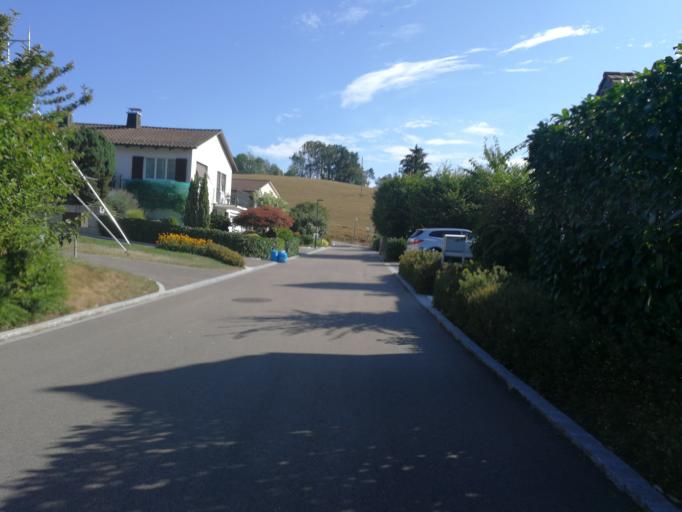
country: CH
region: Zurich
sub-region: Bezirk Uster
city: Esslingen
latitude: 47.2915
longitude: 8.7091
